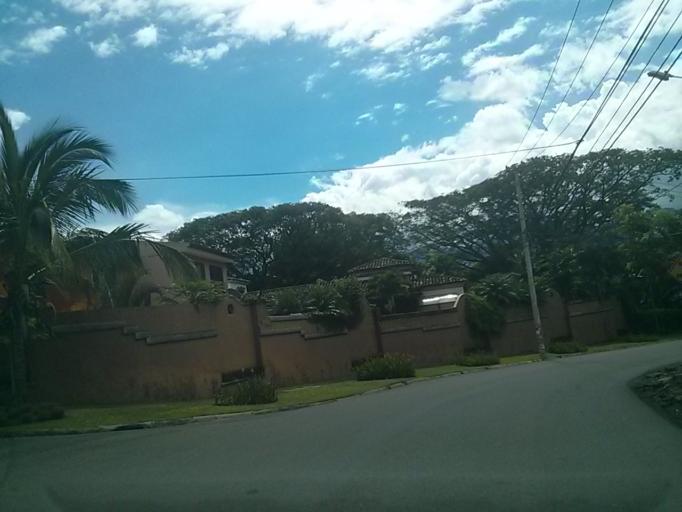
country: CR
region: Heredia
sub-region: Canton de Belen
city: San Antonio
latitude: 9.9632
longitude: -84.1952
